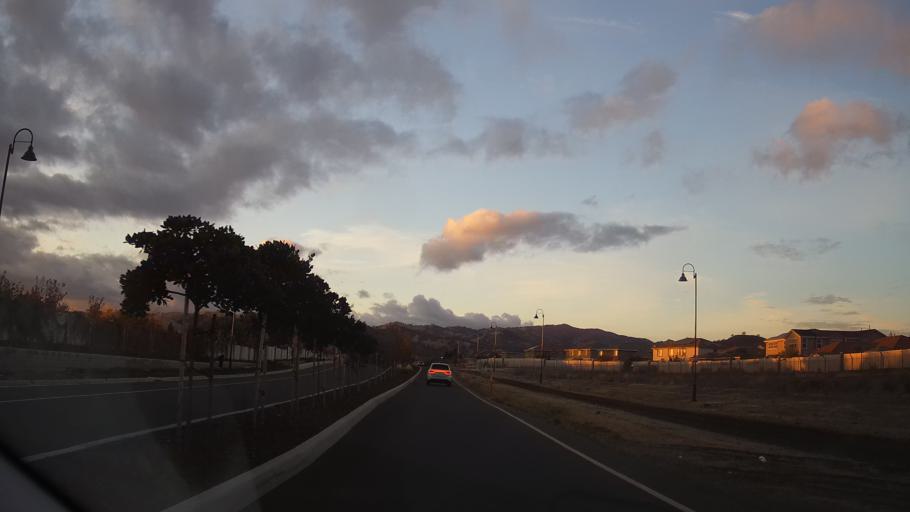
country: US
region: California
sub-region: Solano County
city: Fairfield
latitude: 38.2897
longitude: -122.0118
